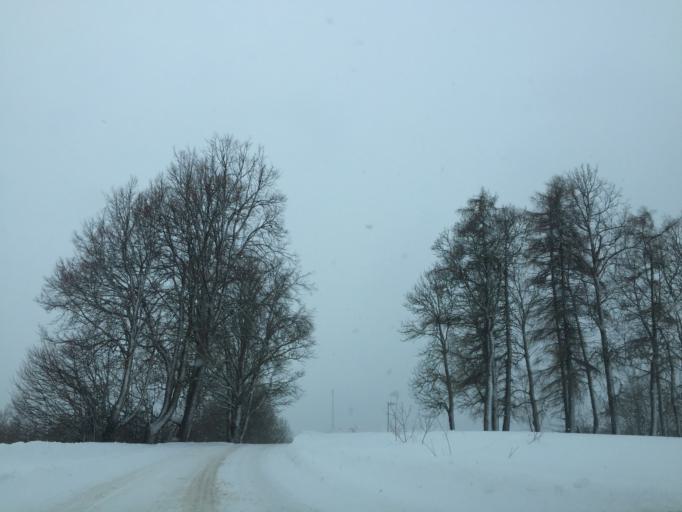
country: LV
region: Amatas Novads
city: Drabesi
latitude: 57.1652
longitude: 25.3322
